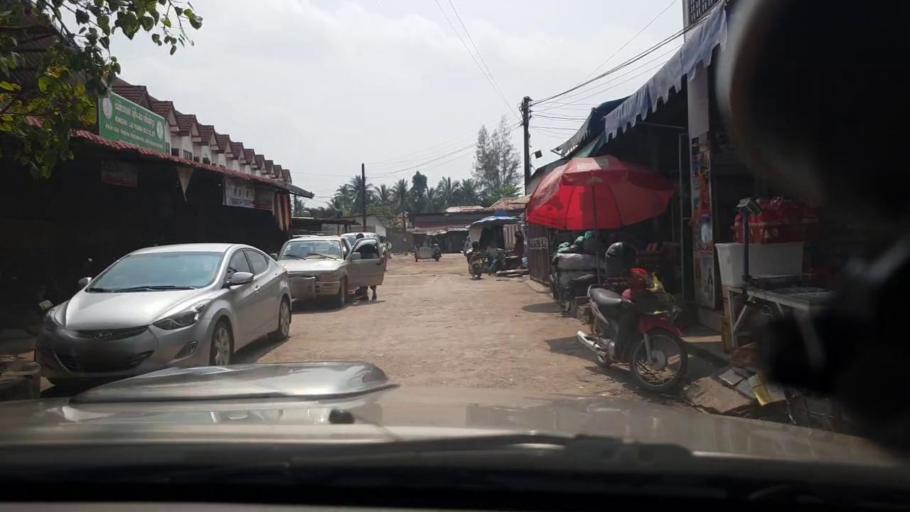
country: TH
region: Nong Khai
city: Si Chiang Mai
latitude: 17.9183
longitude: 102.6202
